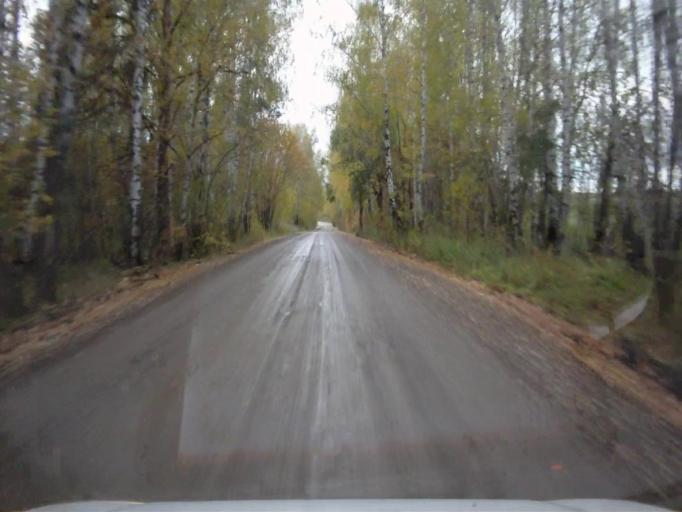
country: RU
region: Sverdlovsk
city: Mikhaylovsk
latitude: 56.1729
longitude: 59.2191
